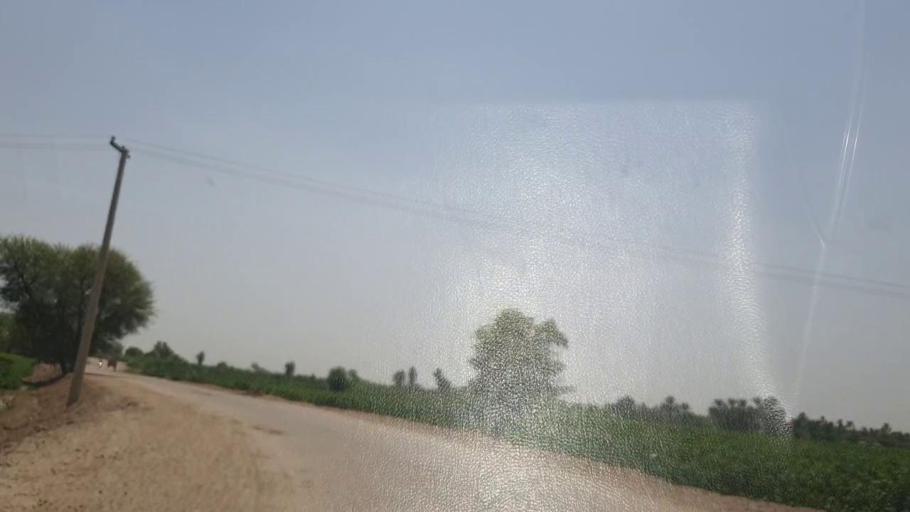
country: PK
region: Sindh
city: Bozdar
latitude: 27.2489
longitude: 68.6751
